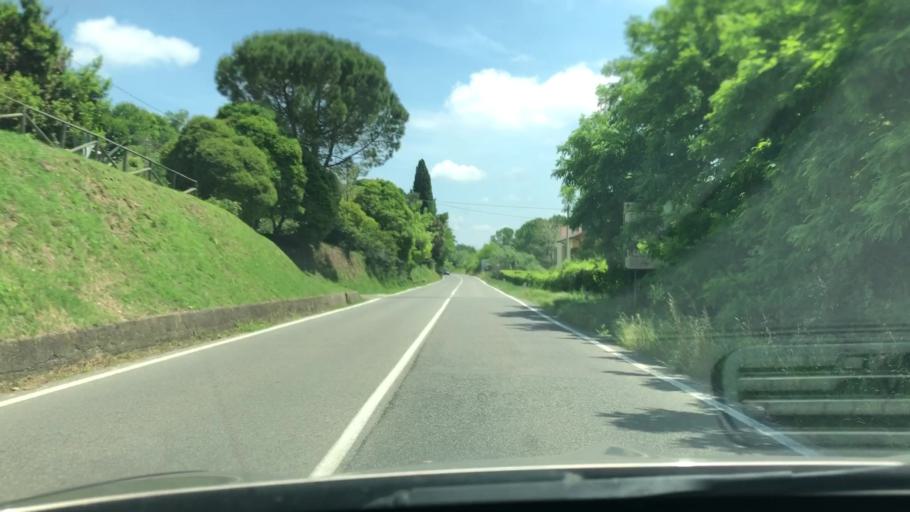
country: IT
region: Tuscany
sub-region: Province of Pisa
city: Forcoli
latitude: 43.6075
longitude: 10.6951
